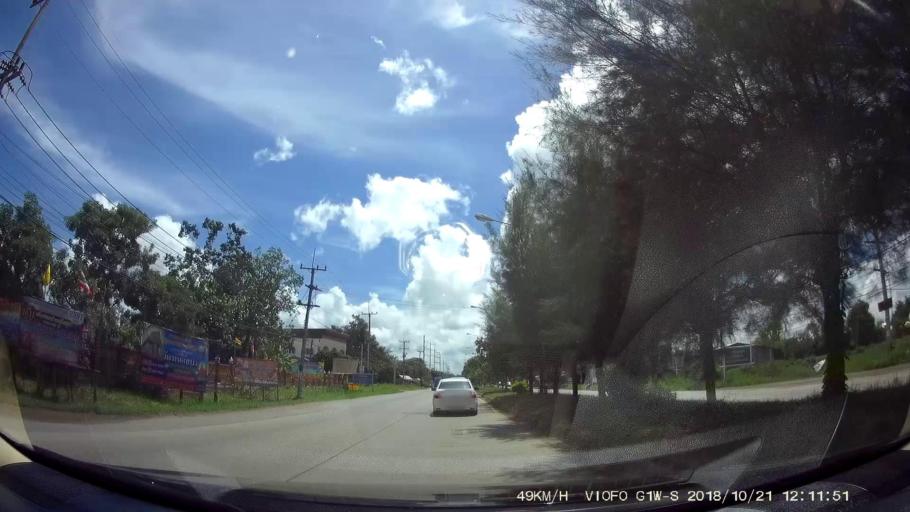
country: TH
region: Chaiyaphum
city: Chatturat
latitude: 15.4125
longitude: 101.8338
